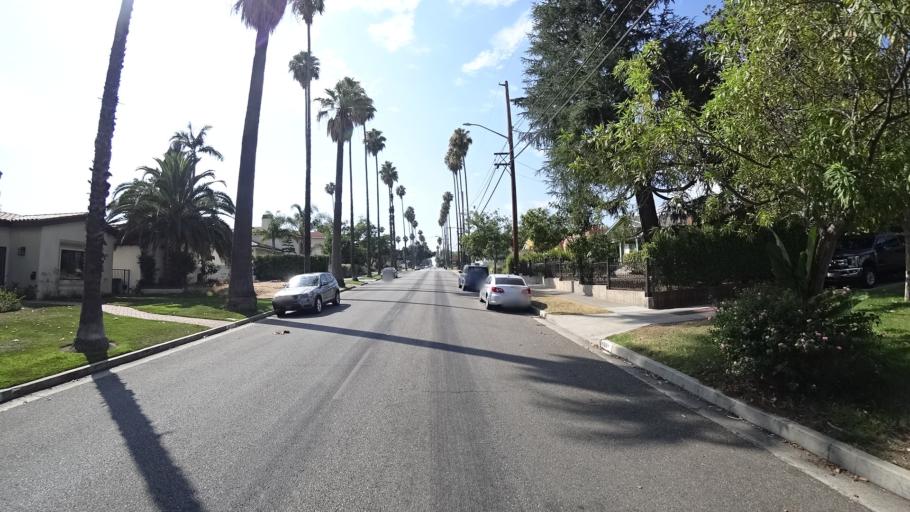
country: US
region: California
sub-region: Los Angeles County
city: Burbank
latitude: 34.1861
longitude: -118.2933
